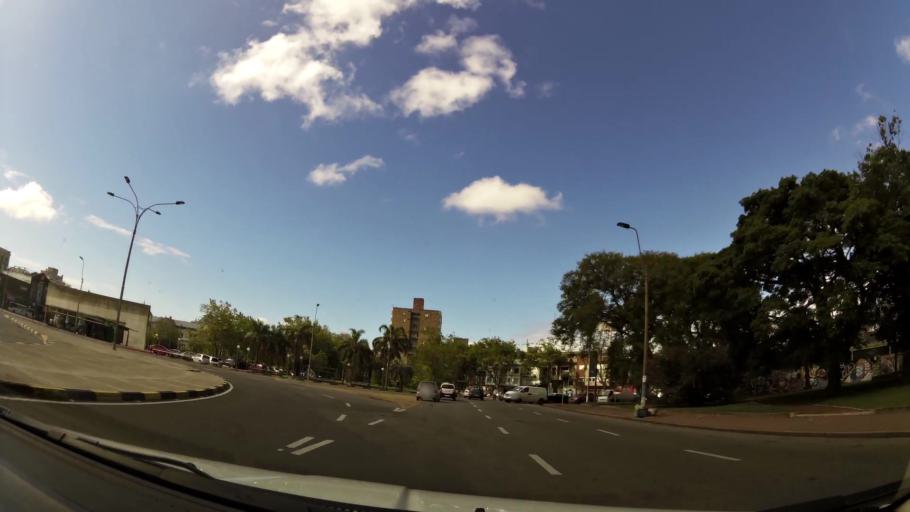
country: UY
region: Montevideo
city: Montevideo
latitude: -34.8910
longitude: -56.1859
